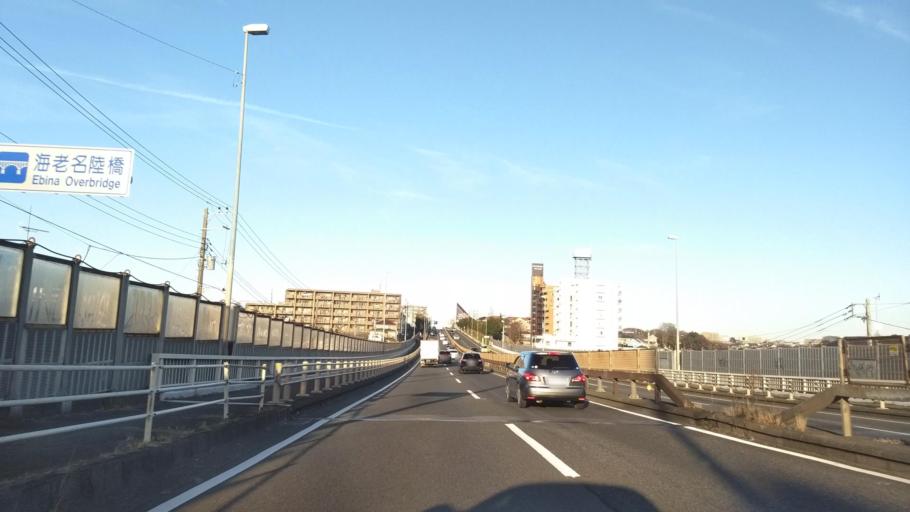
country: JP
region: Kanagawa
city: Zama
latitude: 35.4682
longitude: 139.4078
